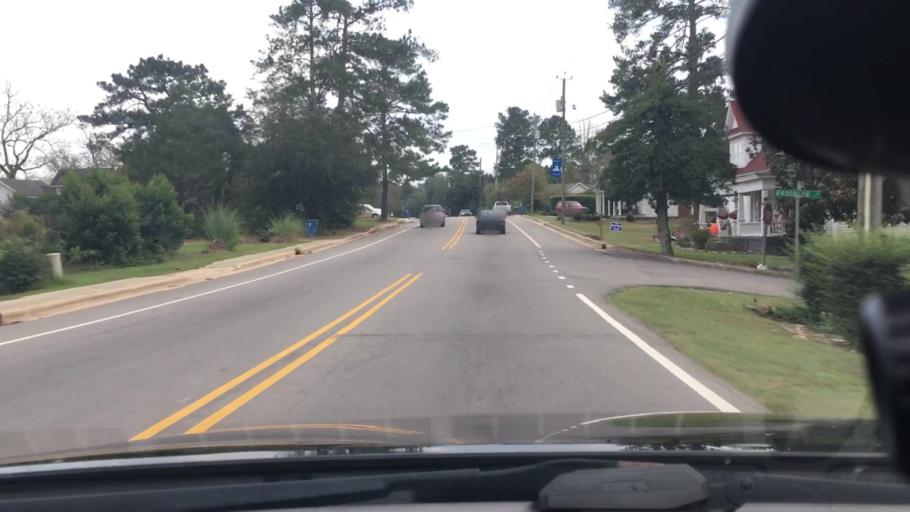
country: US
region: North Carolina
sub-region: Moore County
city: Carthage
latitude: 35.3529
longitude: -79.4228
